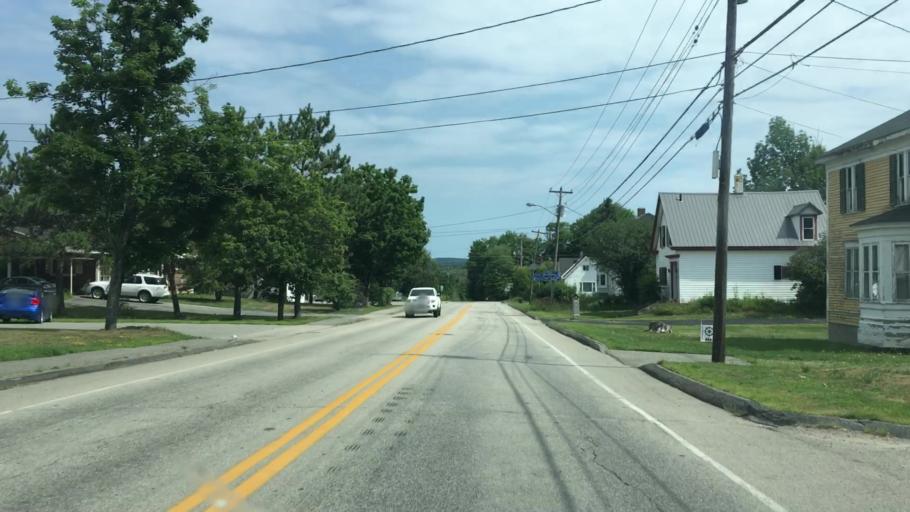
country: US
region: Maine
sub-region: Washington County
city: Calais
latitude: 45.1830
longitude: -67.2686
